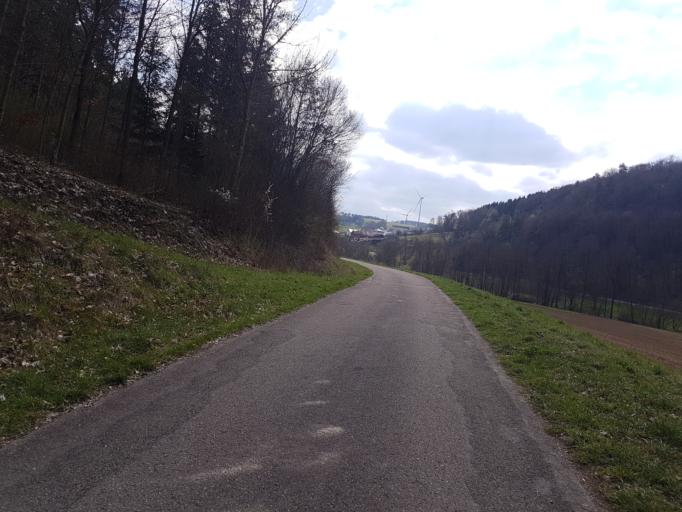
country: DE
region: Baden-Wuerttemberg
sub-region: Regierungsbezirk Stuttgart
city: Krautheim
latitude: 49.3513
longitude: 9.6106
